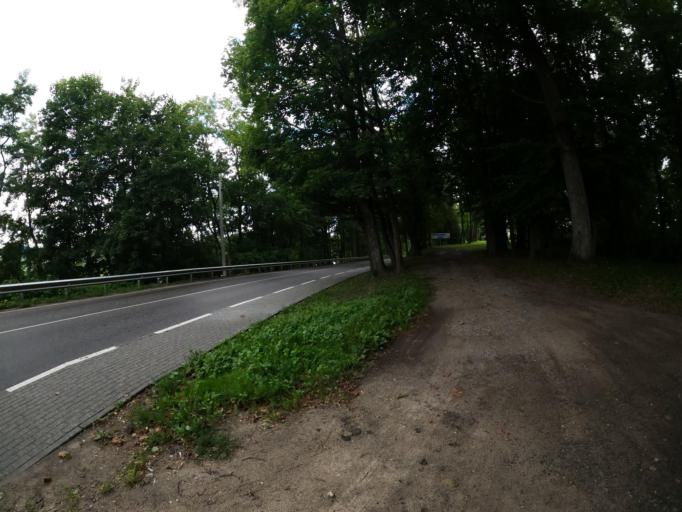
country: RU
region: Kaliningrad
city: Zheleznodorozhnyy
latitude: 54.3617
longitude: 21.3113
